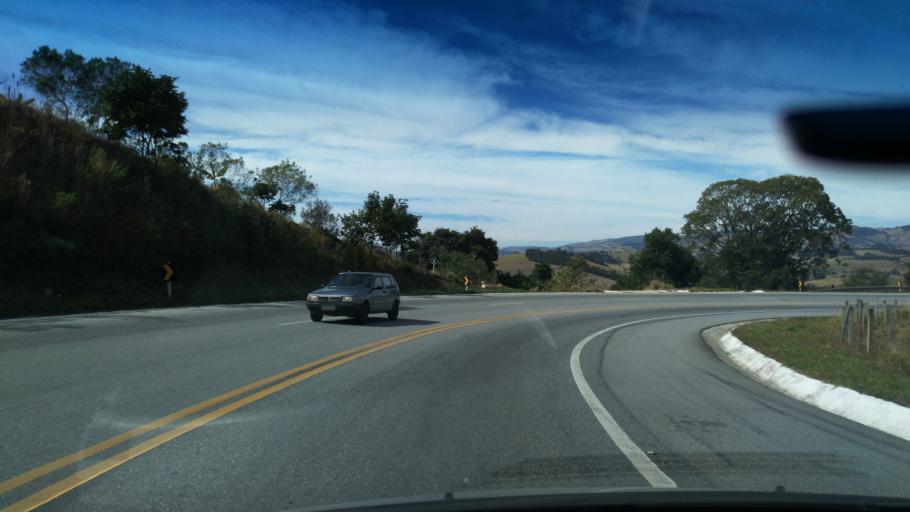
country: BR
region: Minas Gerais
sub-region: Borda Da Mata
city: Borda da Mata
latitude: -22.1297
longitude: -46.1468
